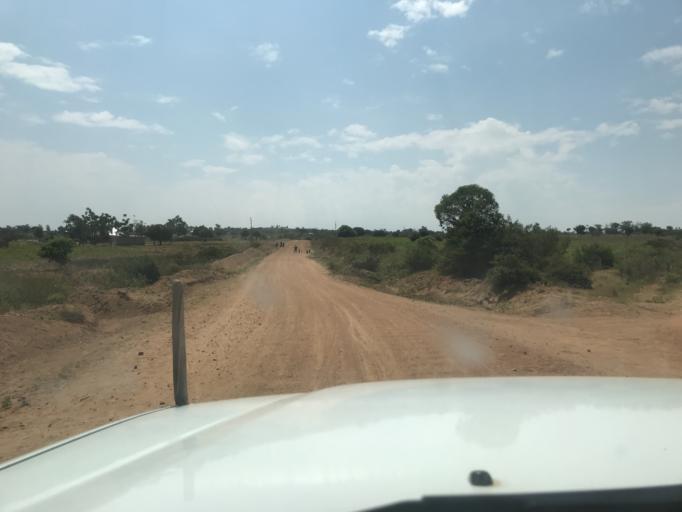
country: TZ
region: Mara
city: Nyamuswa
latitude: -1.9416
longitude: 34.0035
